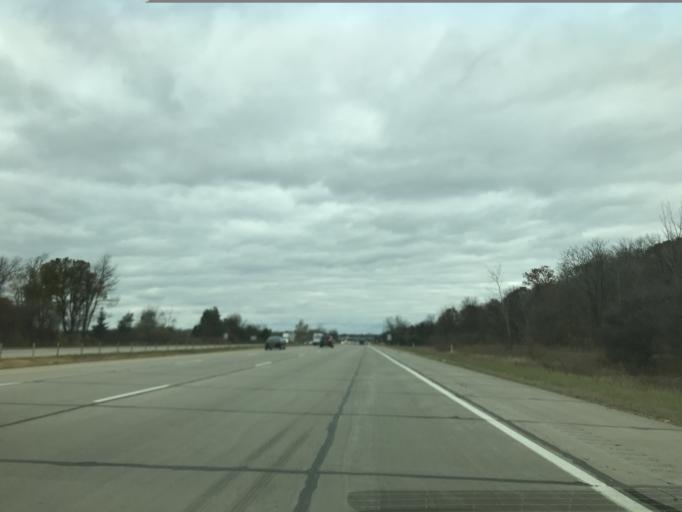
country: US
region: Michigan
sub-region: Eaton County
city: Waverly
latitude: 42.7468
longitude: -84.6677
